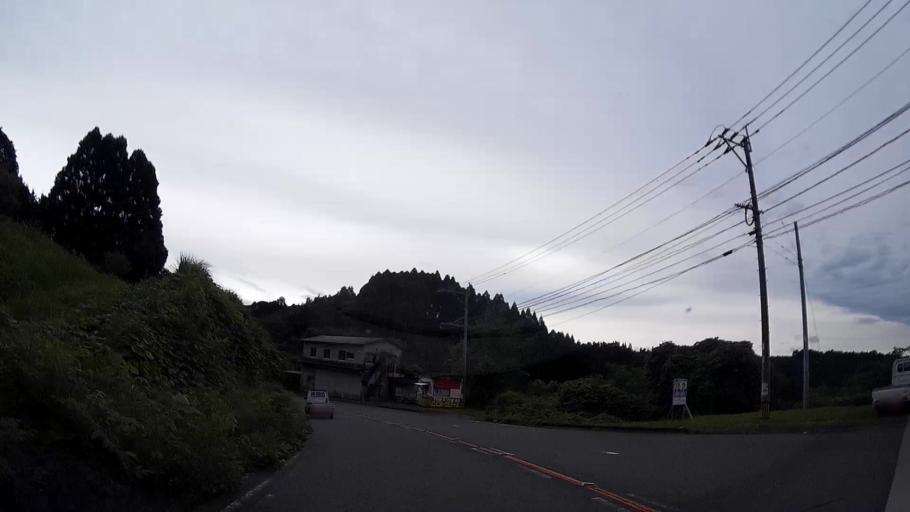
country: JP
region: Kumamoto
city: Kikuchi
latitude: 33.0154
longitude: 130.8697
